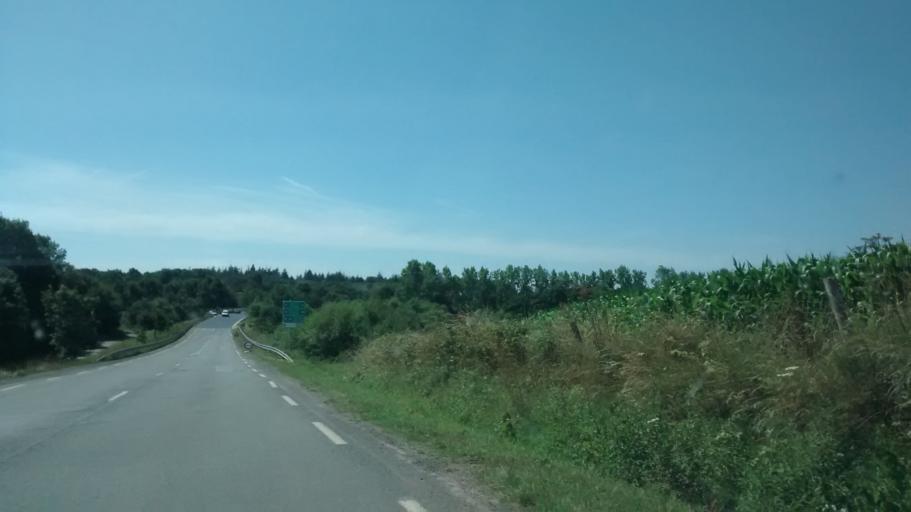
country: FR
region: Brittany
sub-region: Departement du Morbihan
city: Campeneac
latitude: 47.9422
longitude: -2.2856
